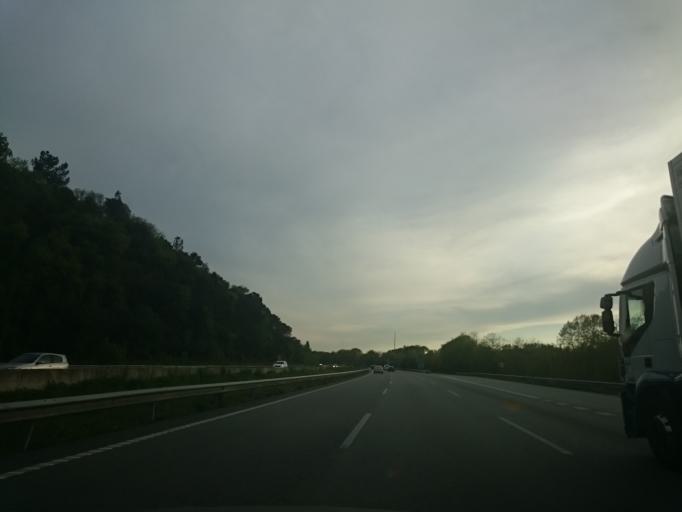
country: ES
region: Catalonia
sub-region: Provincia de Barcelona
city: Sant Celoni
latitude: 41.7031
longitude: 2.5206
